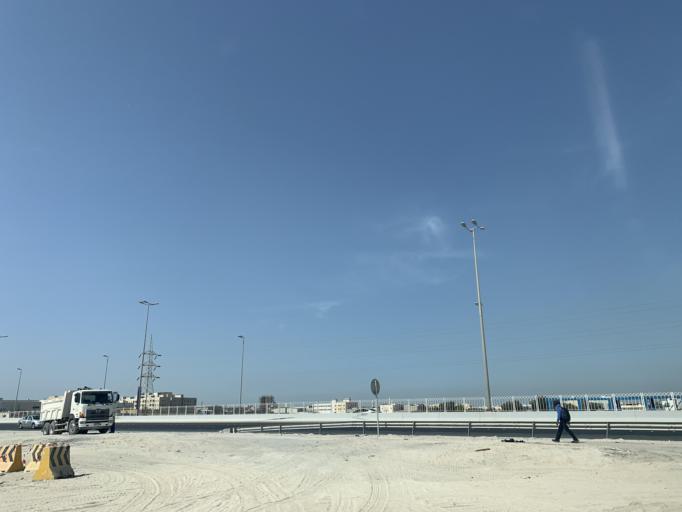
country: BH
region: Northern
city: Ar Rifa'
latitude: 26.1306
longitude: 50.5865
